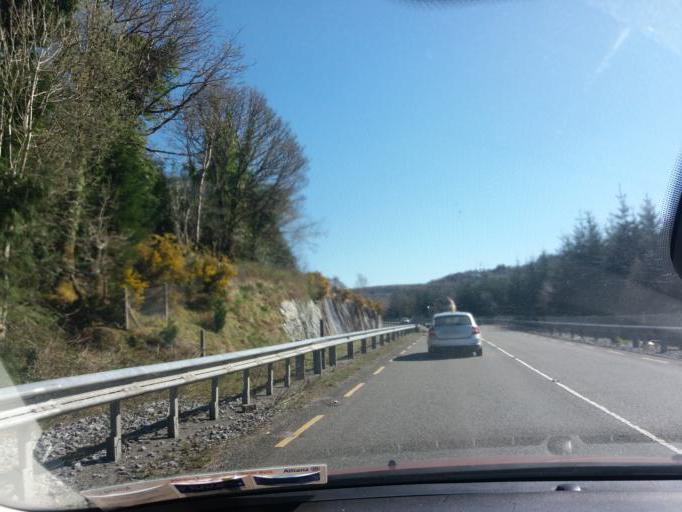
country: IE
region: Munster
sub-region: Ciarrai
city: Cill Airne
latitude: 51.9666
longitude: -9.3539
